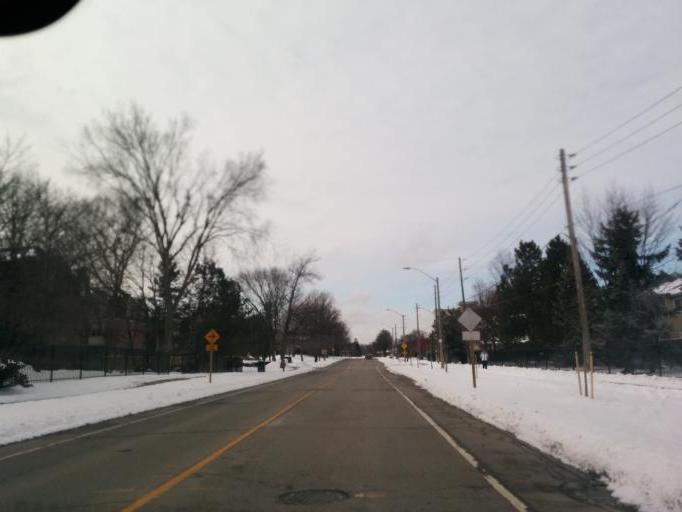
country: CA
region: Ontario
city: Mississauga
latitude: 43.5377
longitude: -79.6708
